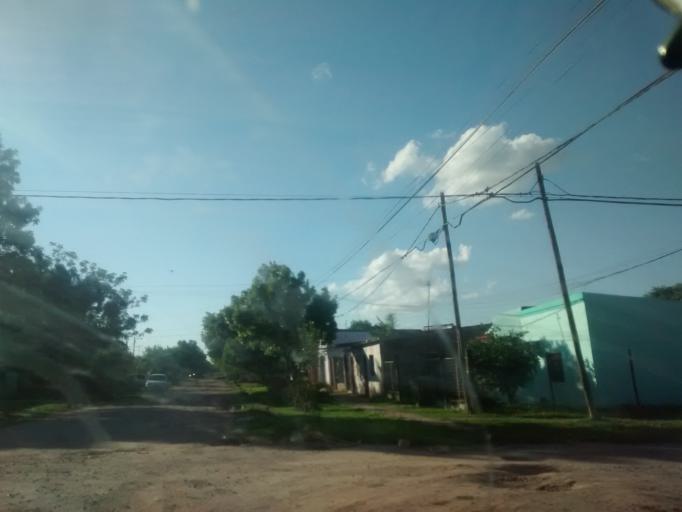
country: AR
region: Chaco
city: Fontana
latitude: -27.4515
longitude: -59.0203
